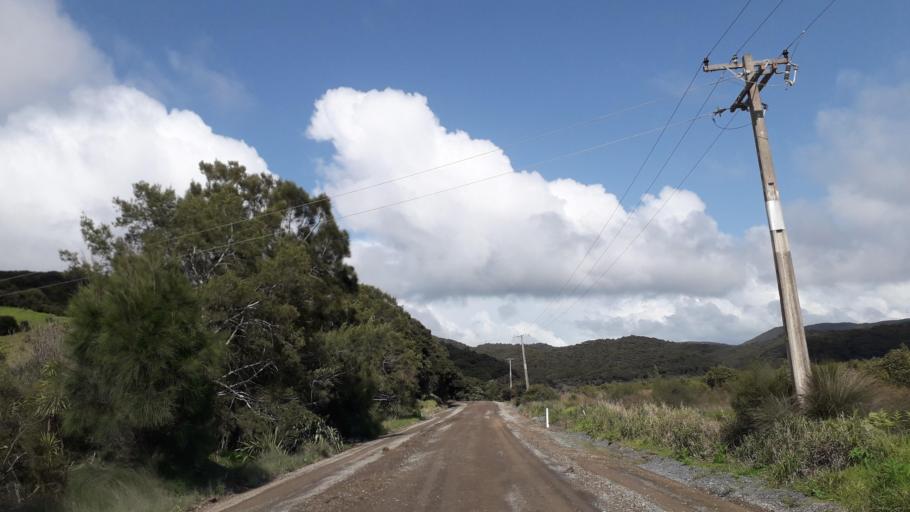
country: NZ
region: Northland
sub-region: Far North District
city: Paihia
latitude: -35.2573
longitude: 174.2672
